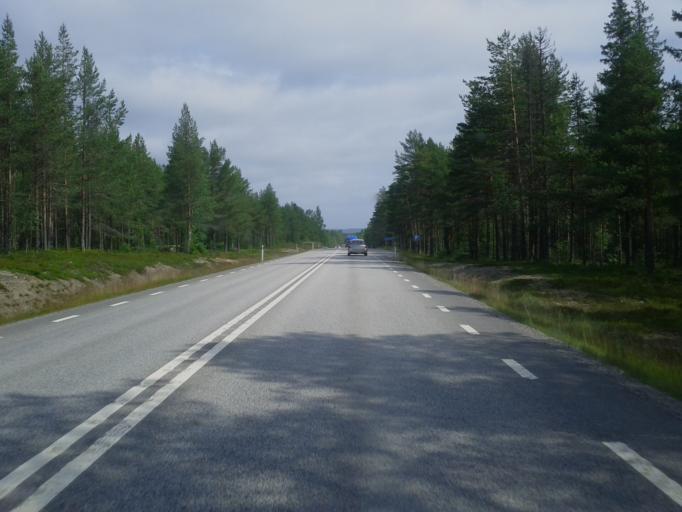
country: SE
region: Vaesterbotten
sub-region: Robertsfors Kommun
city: Robertsfors
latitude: 64.1954
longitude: 21.0057
